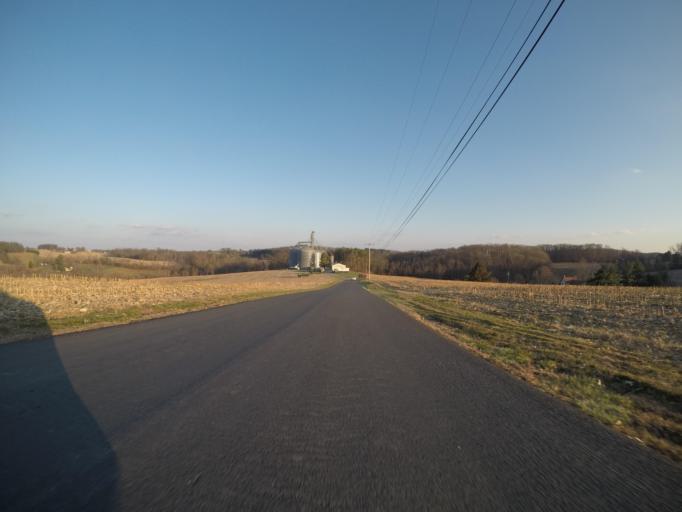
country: US
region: Maryland
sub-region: Carroll County
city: Hampstead
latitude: 39.5837
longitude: -76.8230
